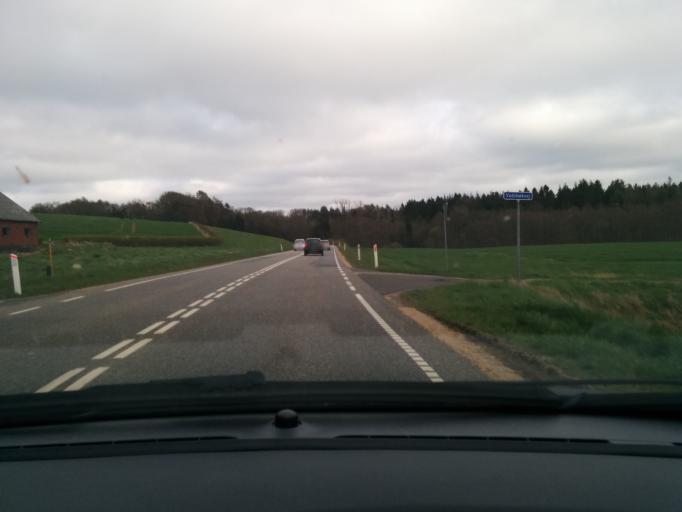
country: DK
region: Central Jutland
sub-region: Favrskov Kommune
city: Hammel
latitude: 56.2139
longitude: 9.7672
